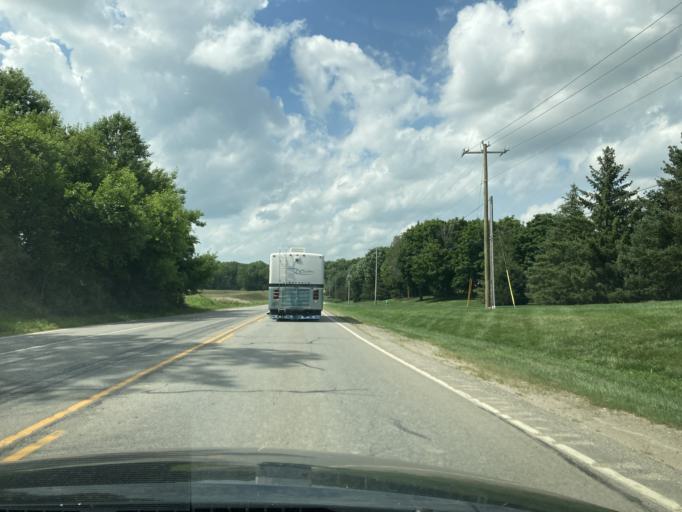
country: US
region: Indiana
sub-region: Boone County
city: Zionsville
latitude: 39.9771
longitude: -86.2543
